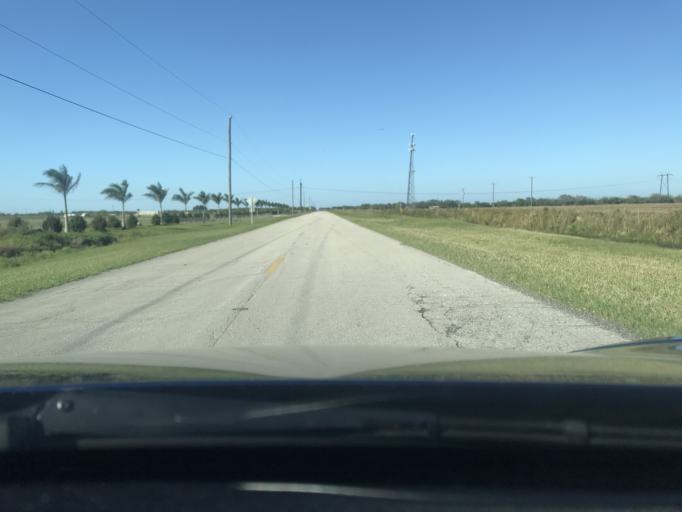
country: US
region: Florida
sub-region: Saint Lucie County
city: Fort Pierce South
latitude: 27.3764
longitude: -80.4976
